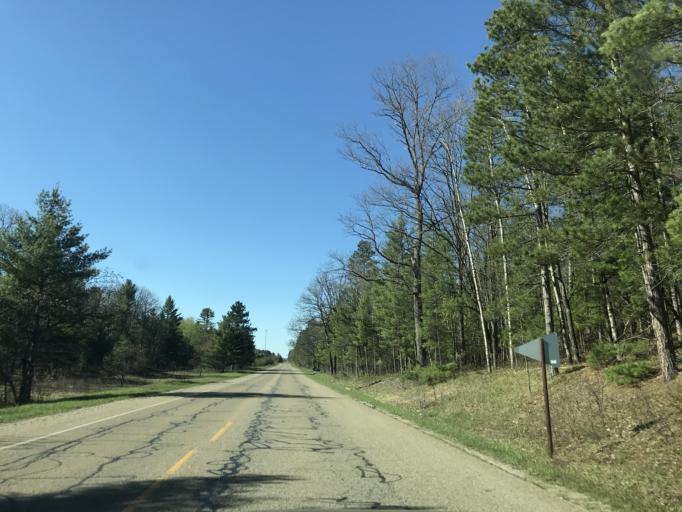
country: US
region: Michigan
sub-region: Crawford County
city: Grayling
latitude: 44.7253
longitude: -84.7477
